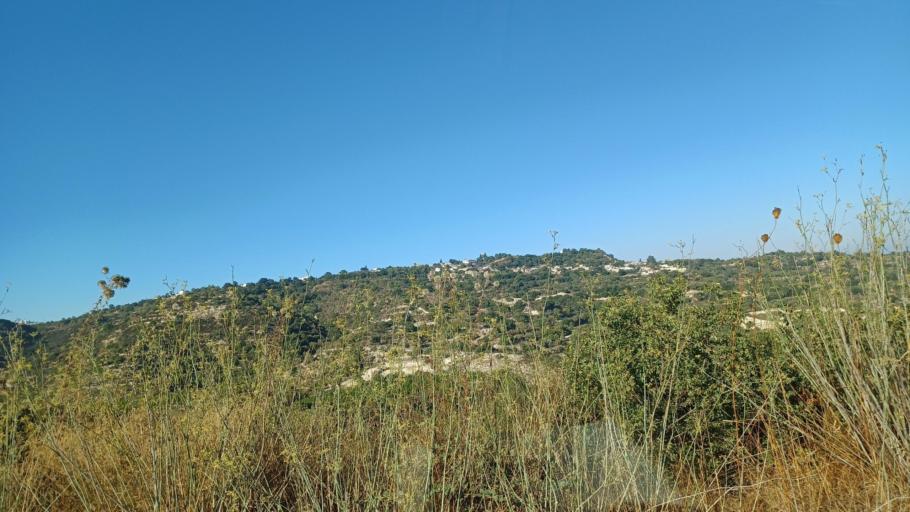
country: CY
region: Pafos
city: Tala
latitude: 34.8643
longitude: 32.4661
